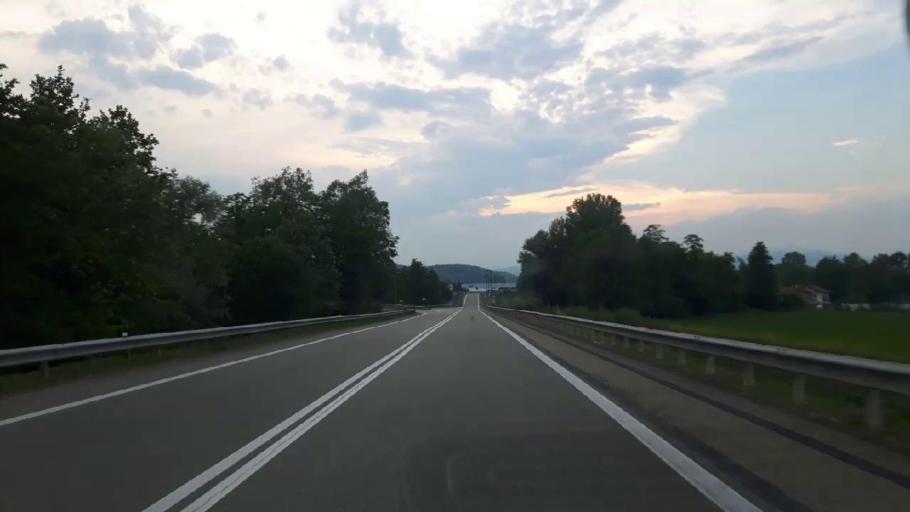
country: IT
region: Lombardy
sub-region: Provincia di Varese
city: Lisanza
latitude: 45.7140
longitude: 8.5957
